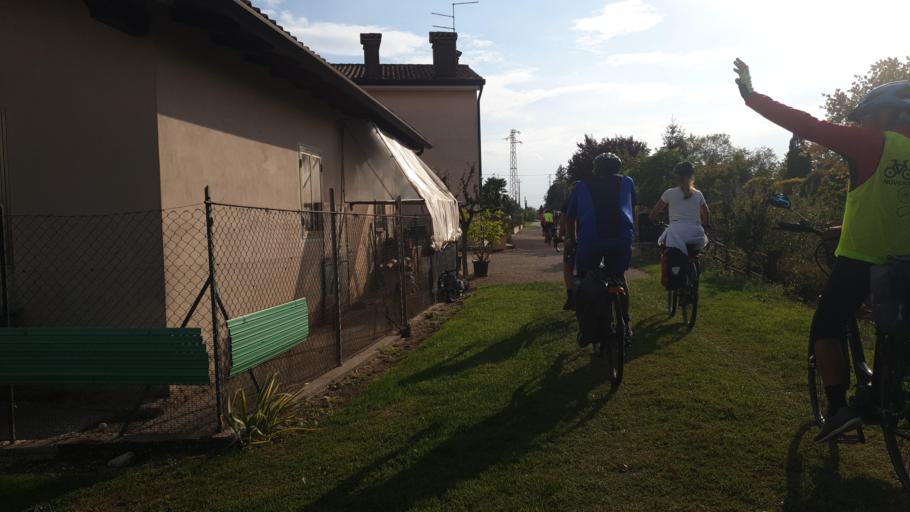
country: IT
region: Veneto
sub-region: Provincia di Vicenza
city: Poiana Maggiore
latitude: 45.2776
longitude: 11.4880
